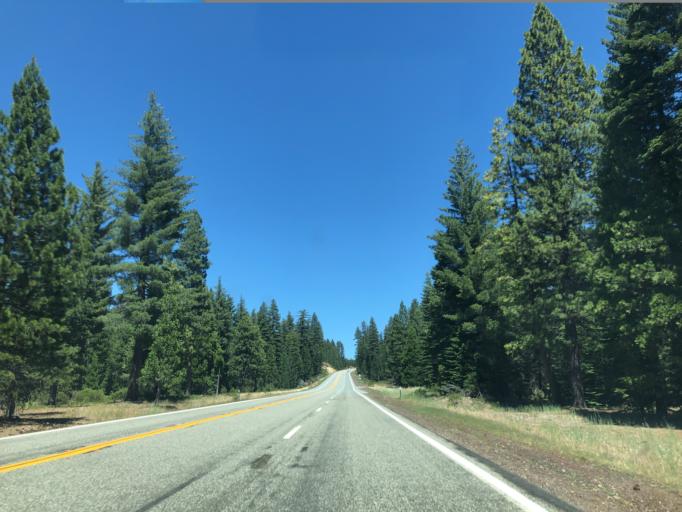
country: US
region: California
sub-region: Shasta County
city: Shingletown
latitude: 40.5341
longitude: -121.6183
